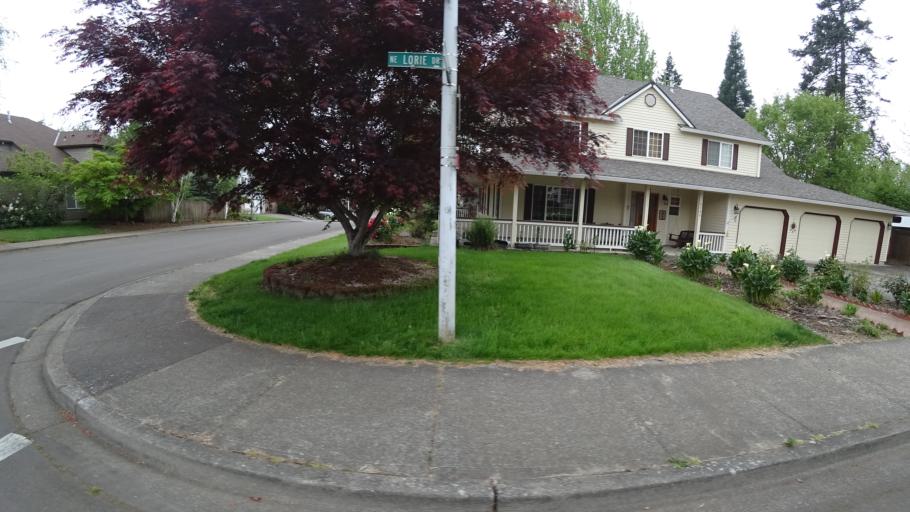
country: US
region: Oregon
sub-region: Washington County
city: Hillsboro
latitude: 45.5446
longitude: -122.9829
